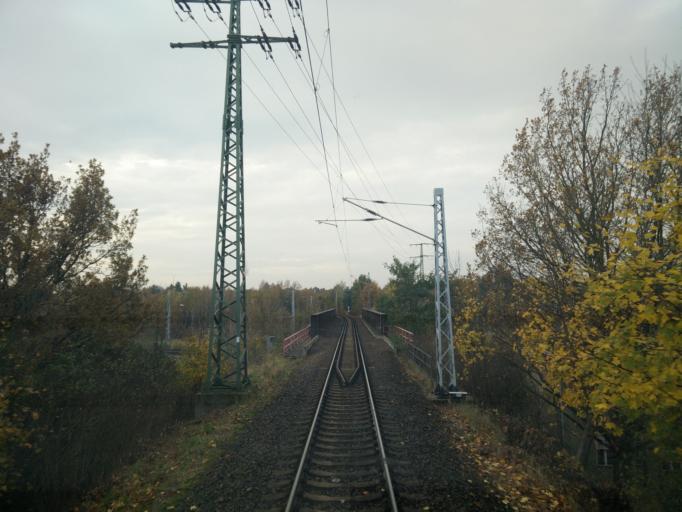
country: DE
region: Berlin
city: Adlershof
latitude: 52.4242
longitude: 13.5593
